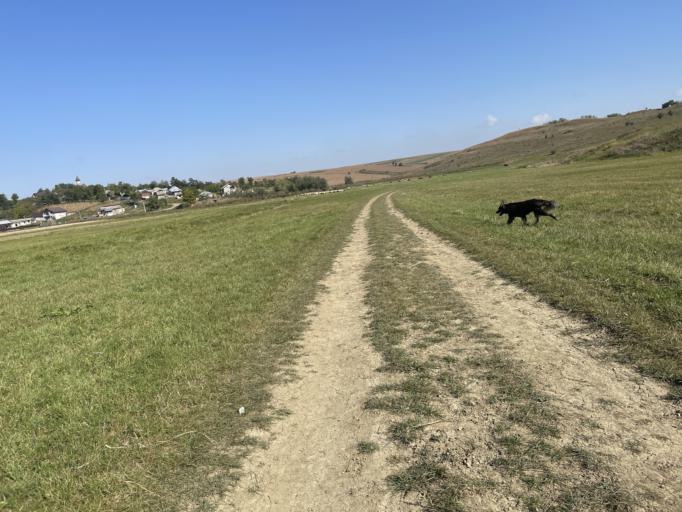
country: RO
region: Iasi
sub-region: Comuna Dumesti
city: Pausesti
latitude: 47.1586
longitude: 27.3091
